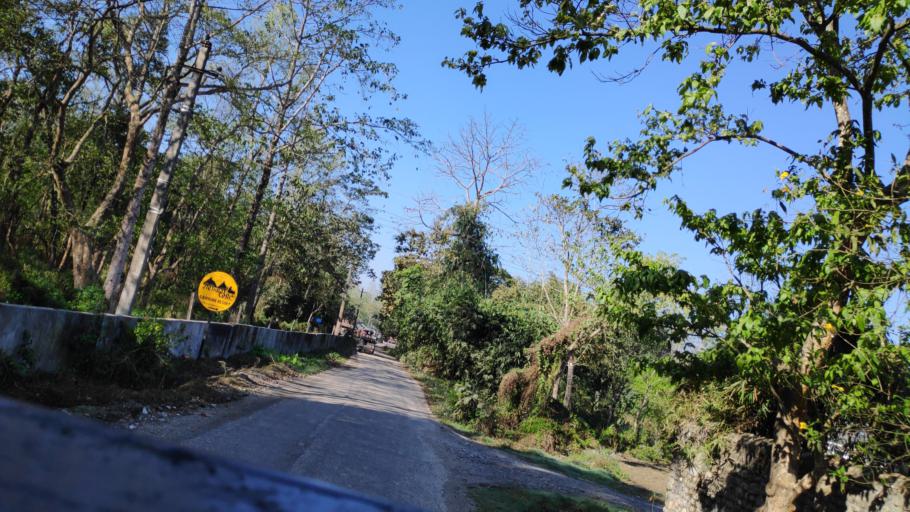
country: NP
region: Central Region
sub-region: Narayani Zone
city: Bharatpur
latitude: 27.5746
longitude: 84.5125
